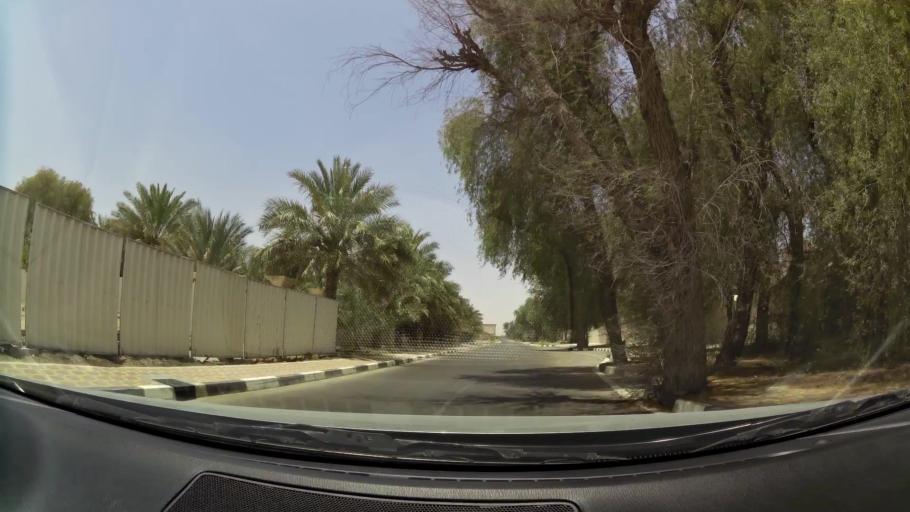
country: OM
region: Al Buraimi
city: Al Buraymi
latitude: 24.2831
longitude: 55.7373
